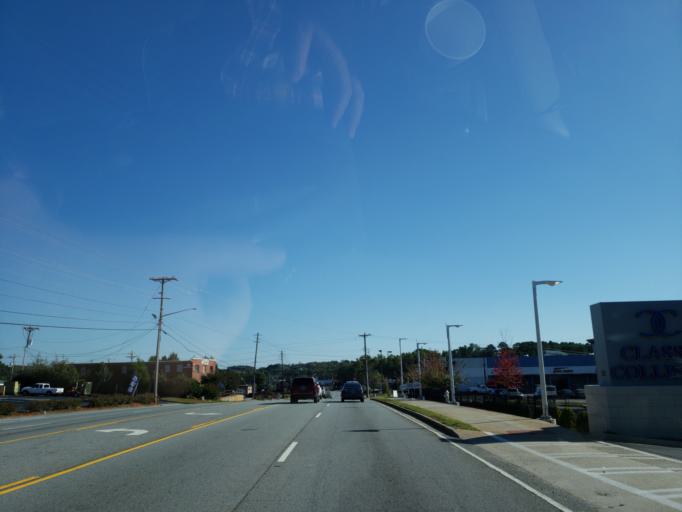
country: US
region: Georgia
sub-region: Gwinnett County
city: Lawrenceville
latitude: 33.9643
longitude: -84.0079
